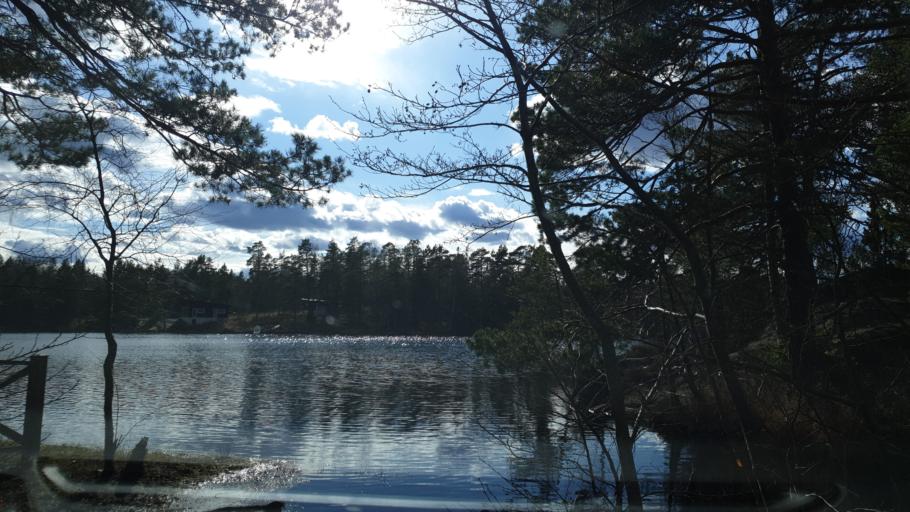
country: SE
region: Stockholm
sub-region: Tyreso Kommun
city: Brevik
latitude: 59.2641
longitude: 18.4197
